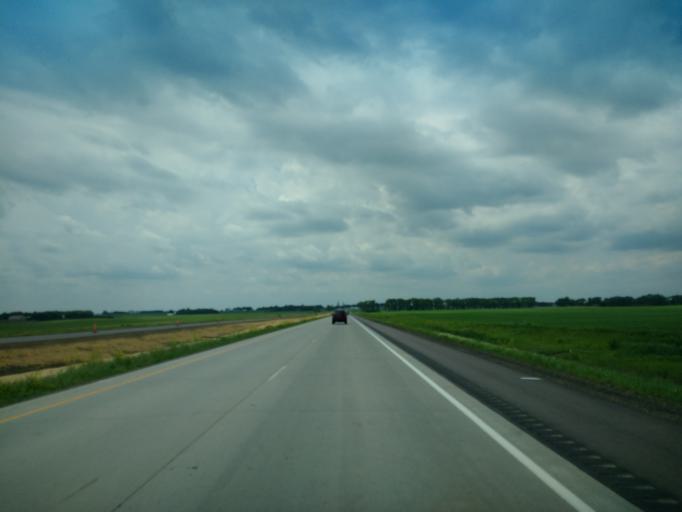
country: US
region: Minnesota
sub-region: Cottonwood County
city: Mountain Lake
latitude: 43.9171
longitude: -95.0058
